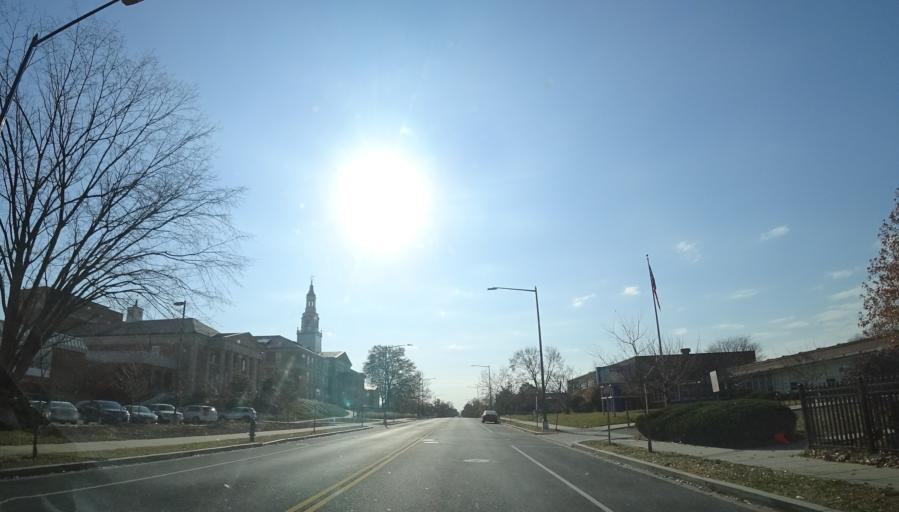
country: US
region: Maryland
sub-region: Montgomery County
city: Takoma Park
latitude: 38.9449
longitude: -77.0301
